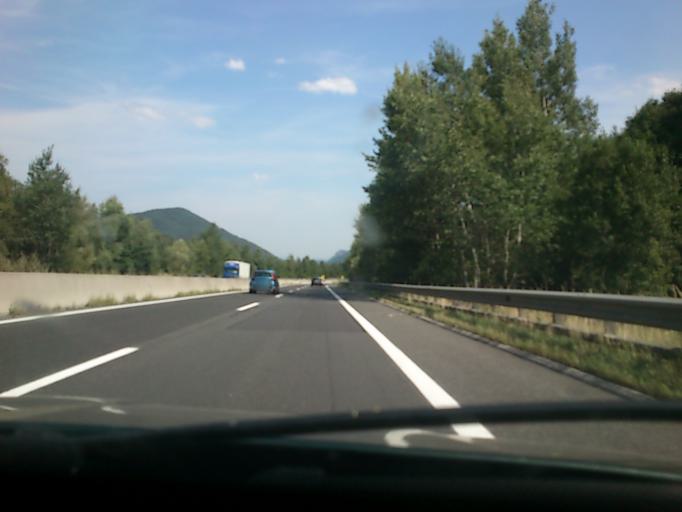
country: AT
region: Lower Austria
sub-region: Politischer Bezirk Neunkirchen
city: Edlitz
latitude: 47.5974
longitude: 16.1242
